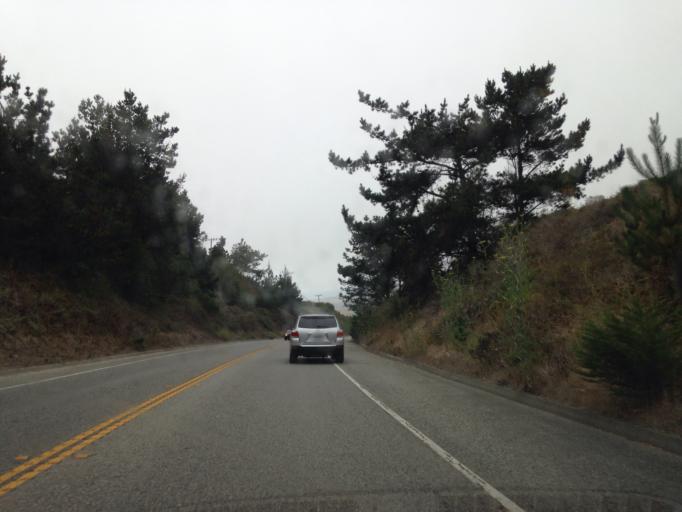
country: US
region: California
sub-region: San Mateo County
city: Half Moon Bay
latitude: 37.3462
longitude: -122.3966
